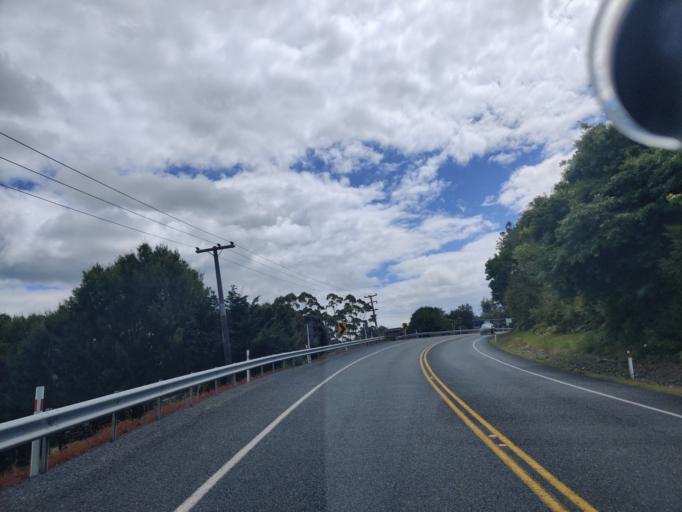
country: NZ
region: Northland
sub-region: Far North District
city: Paihia
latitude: -35.2915
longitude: 174.0098
